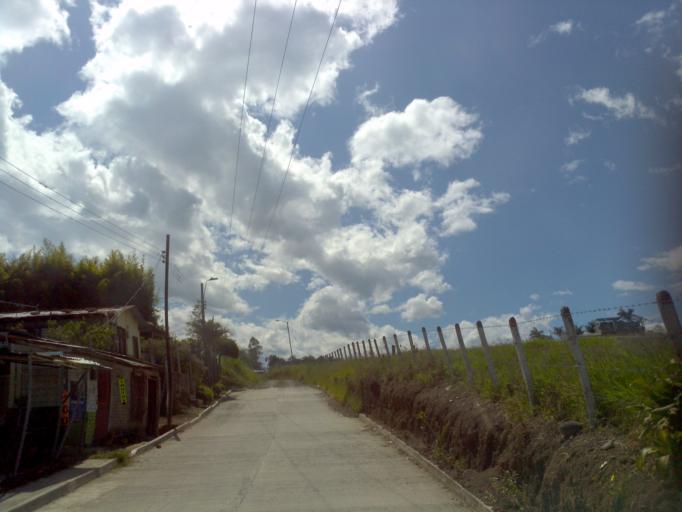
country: CO
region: Valle del Cauca
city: Ulloa
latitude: 4.7241
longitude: -75.7007
